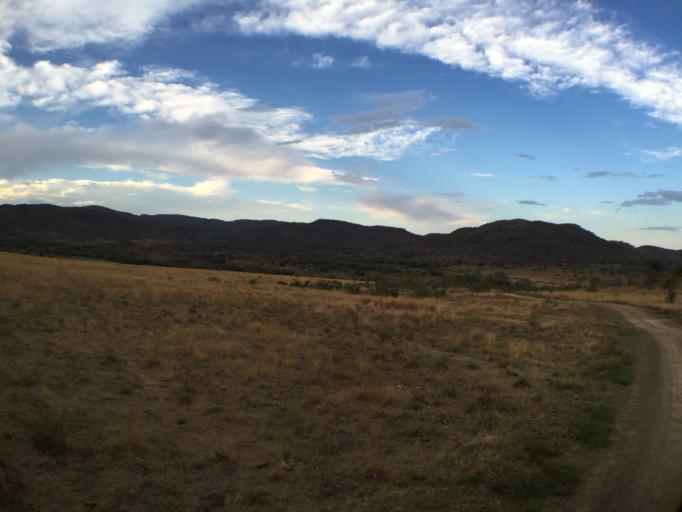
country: ZA
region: North-West
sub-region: Bojanala Platinum District Municipality
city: Mogwase
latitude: -25.2282
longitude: 27.0760
